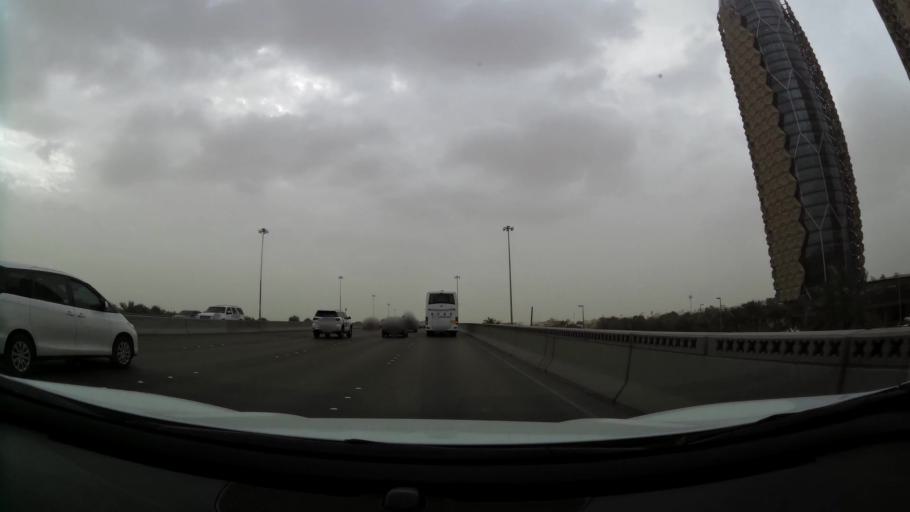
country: AE
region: Abu Dhabi
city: Abu Dhabi
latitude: 24.4571
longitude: 54.4019
